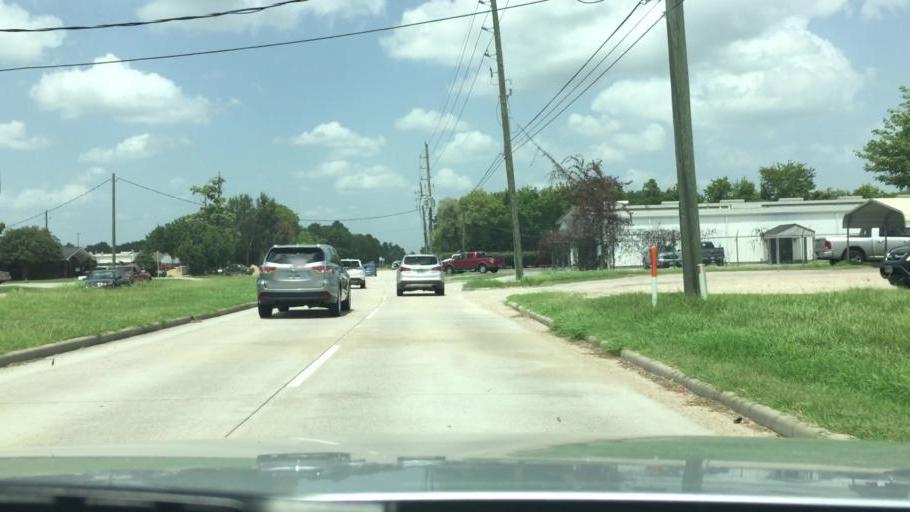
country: US
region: Texas
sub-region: Harris County
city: Hudson
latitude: 29.9630
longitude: -95.5295
